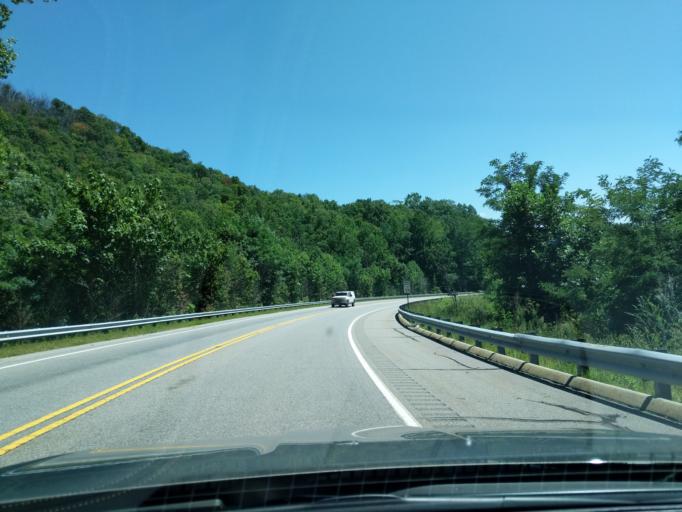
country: US
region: North Carolina
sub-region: Macon County
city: Franklin
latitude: 35.1308
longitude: -83.5349
